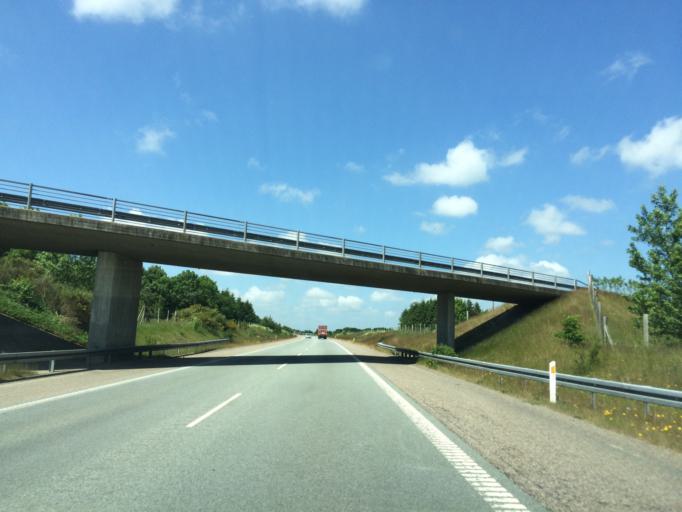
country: DK
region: Central Jutland
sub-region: Herning Kommune
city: Herning
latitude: 56.1825
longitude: 8.9693
